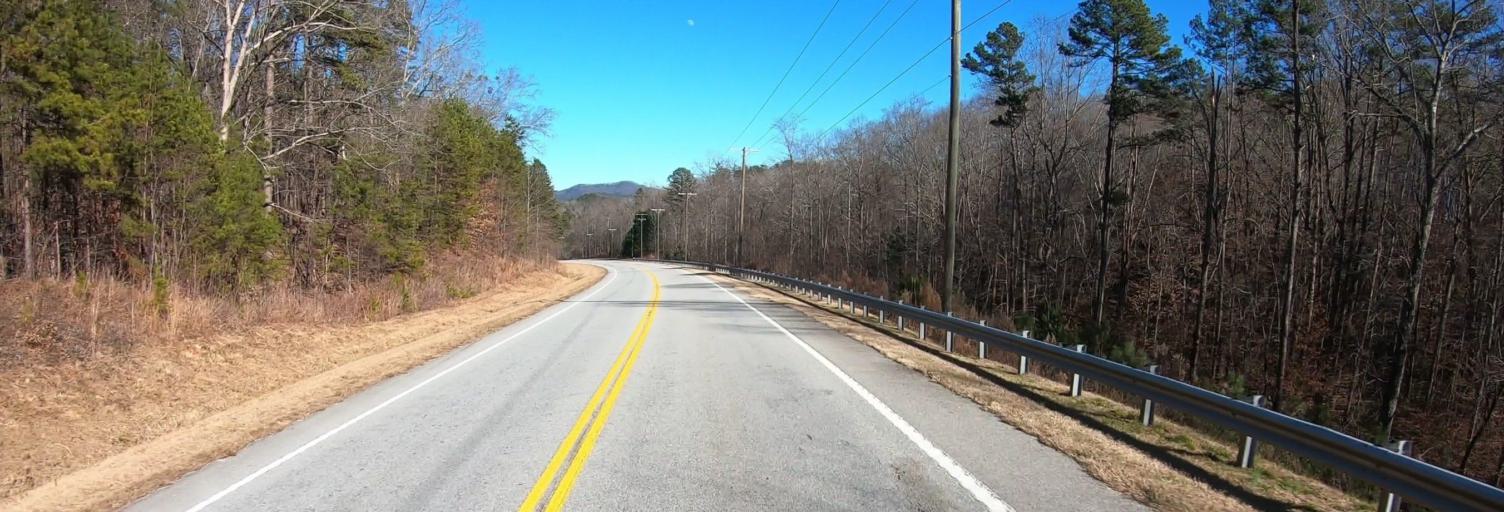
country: US
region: South Carolina
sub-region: Oconee County
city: Walhalla
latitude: 34.9151
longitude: -82.9183
